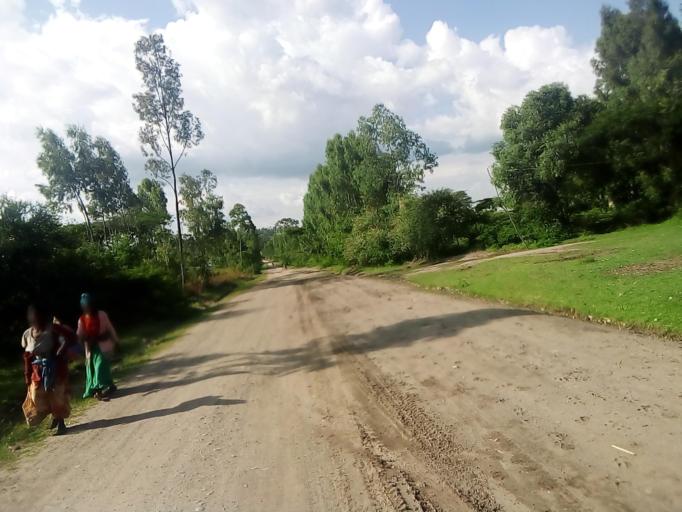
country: ET
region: Southern Nations, Nationalities, and People's Region
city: K'olito
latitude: 7.6597
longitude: 38.0478
